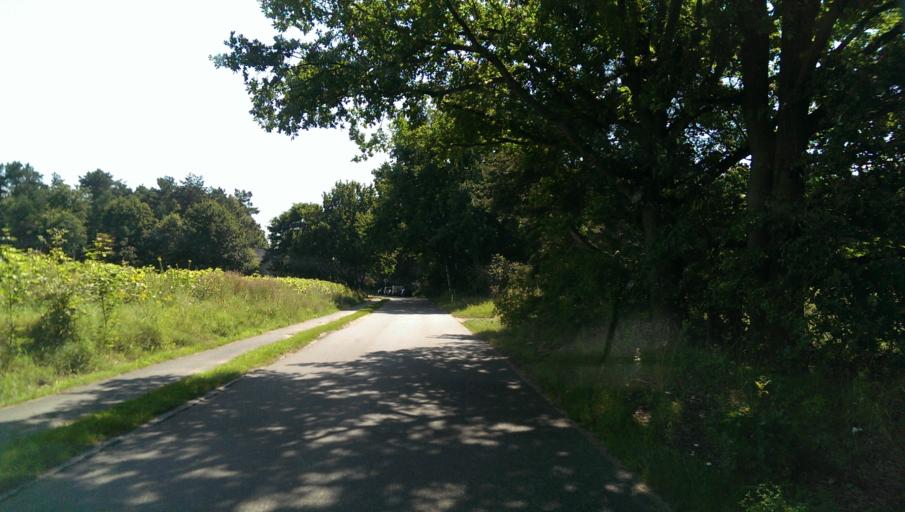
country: DE
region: Brandenburg
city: Michendorf
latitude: 52.2976
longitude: 13.0621
